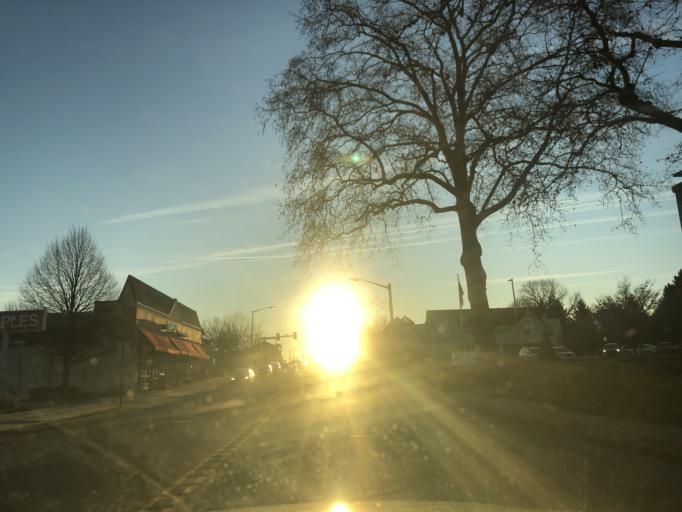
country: US
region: Pennsylvania
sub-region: Montgomery County
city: Bryn Mawr
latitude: 40.0203
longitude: -75.3159
